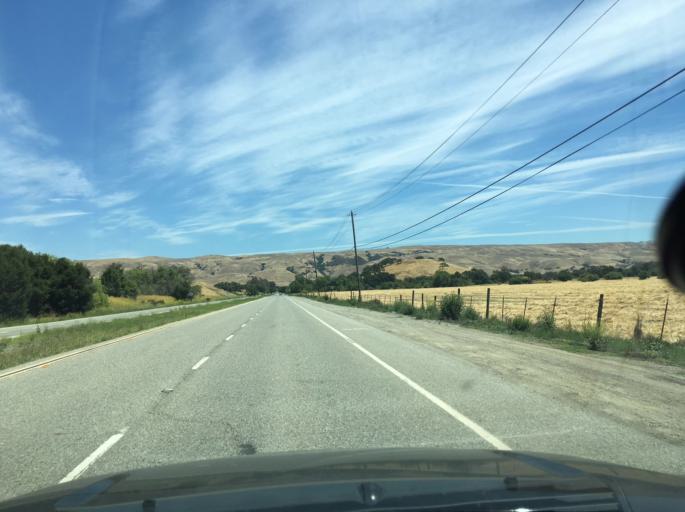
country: US
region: California
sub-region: Santa Clara County
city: Morgan Hill
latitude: 37.1941
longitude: -121.7465
